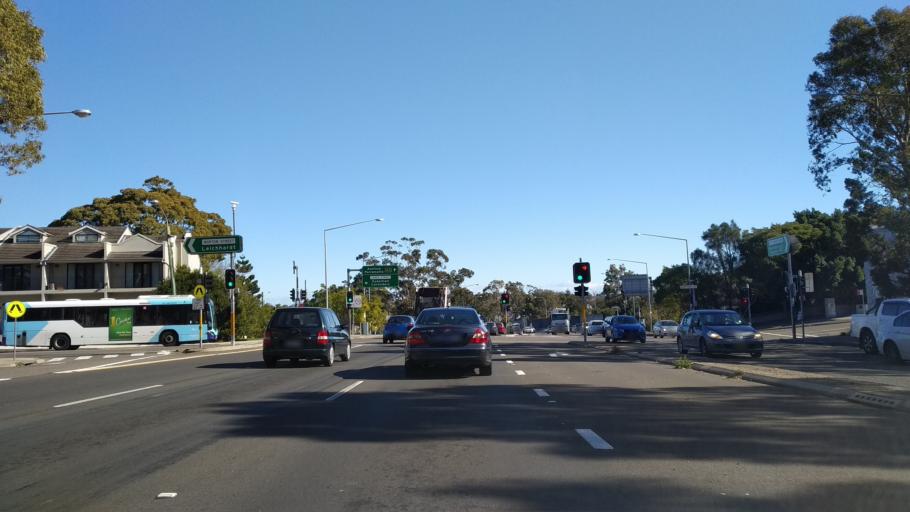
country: AU
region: New South Wales
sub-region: Leichhardt
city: Leichhardt
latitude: -33.8752
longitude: 151.1566
